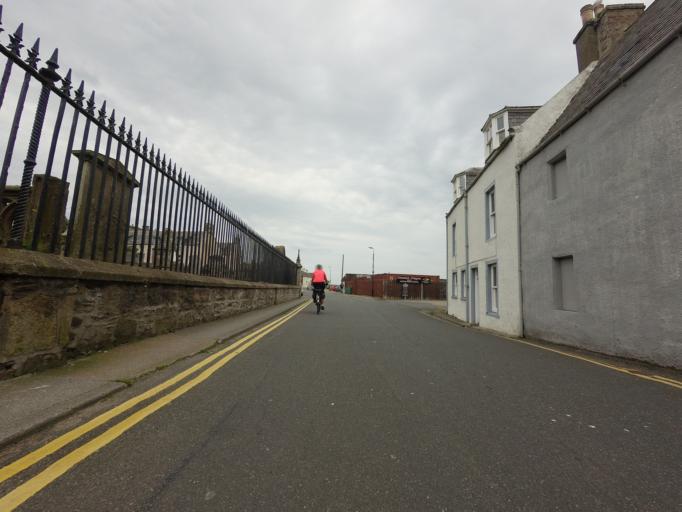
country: GB
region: Scotland
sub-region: Aberdeenshire
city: Banff
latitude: 57.6652
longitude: -2.5198
